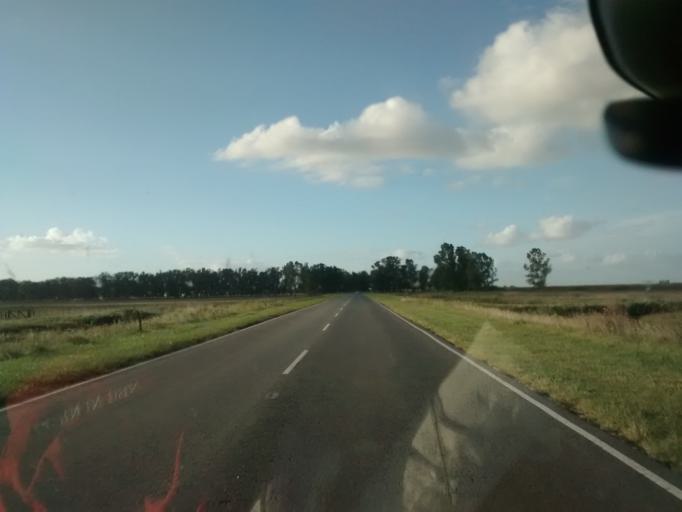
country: AR
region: Buenos Aires
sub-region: Partido de General Belgrano
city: General Belgrano
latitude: -36.1511
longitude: -58.5953
